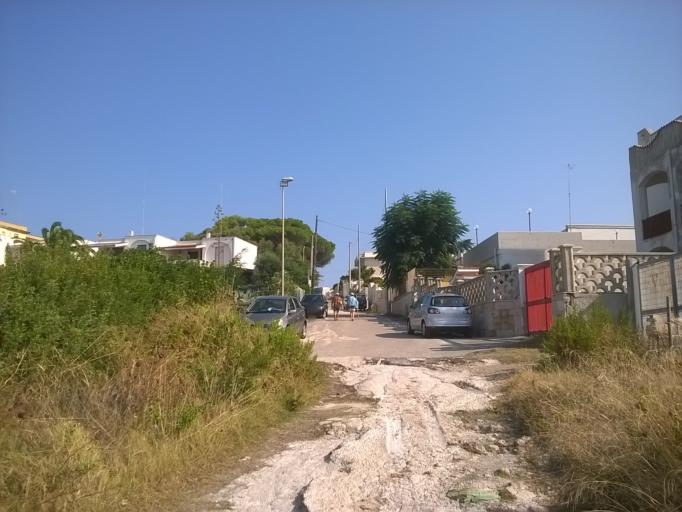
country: IT
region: Apulia
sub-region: Provincia di Taranto
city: Taranto
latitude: 40.3965
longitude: 17.2558
